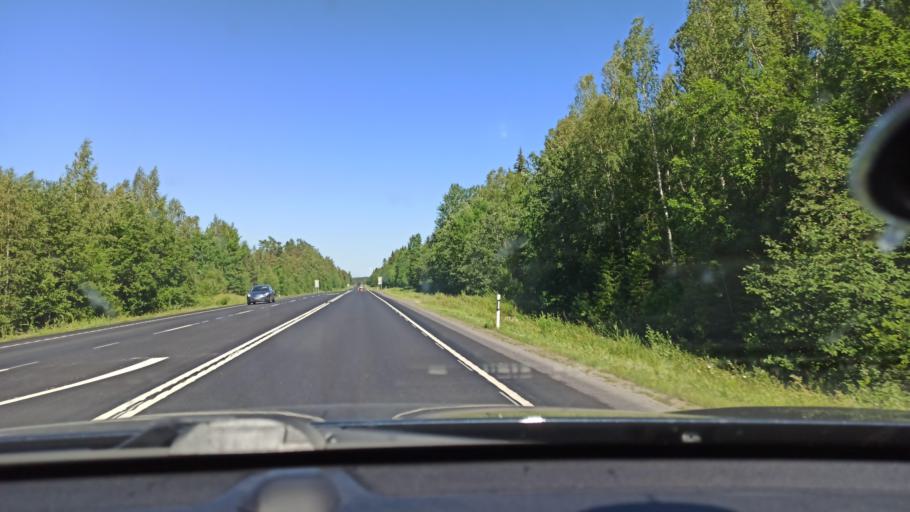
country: FI
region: Ostrobothnia
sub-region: Vaasa
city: Oravais
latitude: 63.2712
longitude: 22.3141
